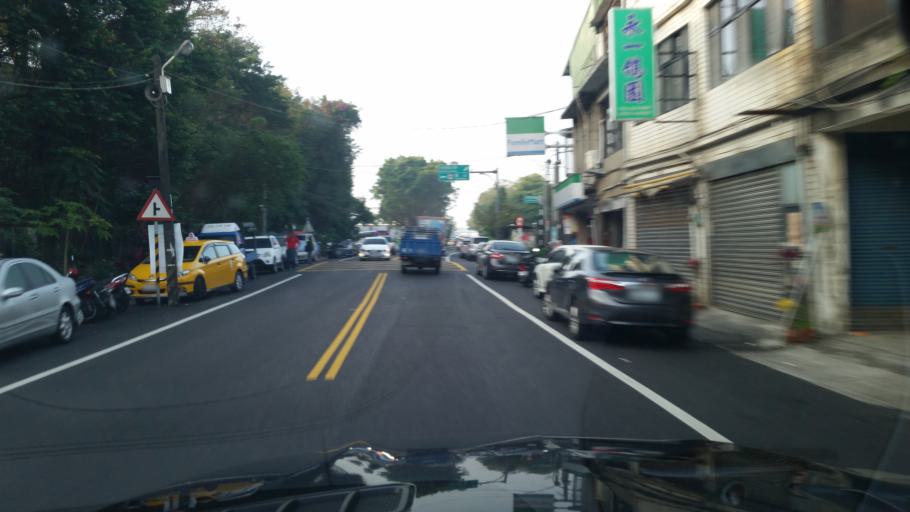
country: TW
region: Taiwan
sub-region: Taoyuan
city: Taoyuan
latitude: 25.0606
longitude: 121.3585
